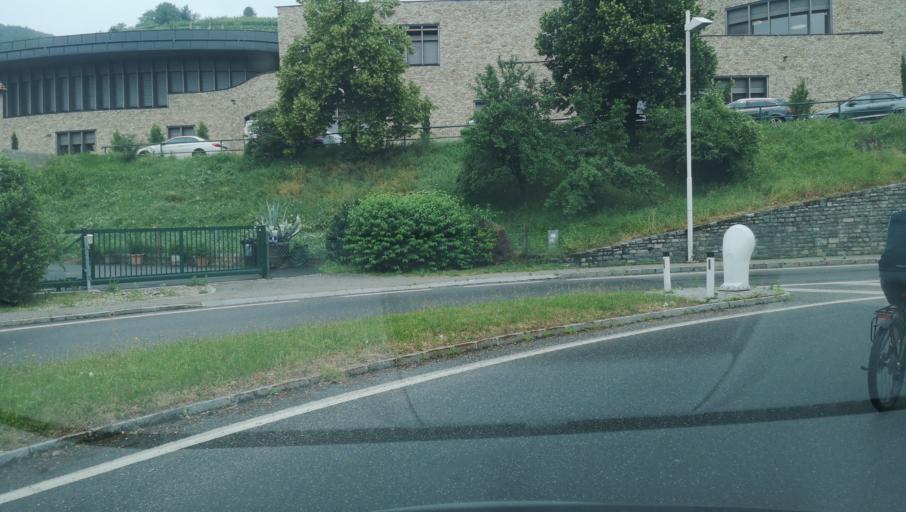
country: AT
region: Lower Austria
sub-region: Politischer Bezirk Krems
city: Weinzierl bei Krems
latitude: 48.3984
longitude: 15.5709
